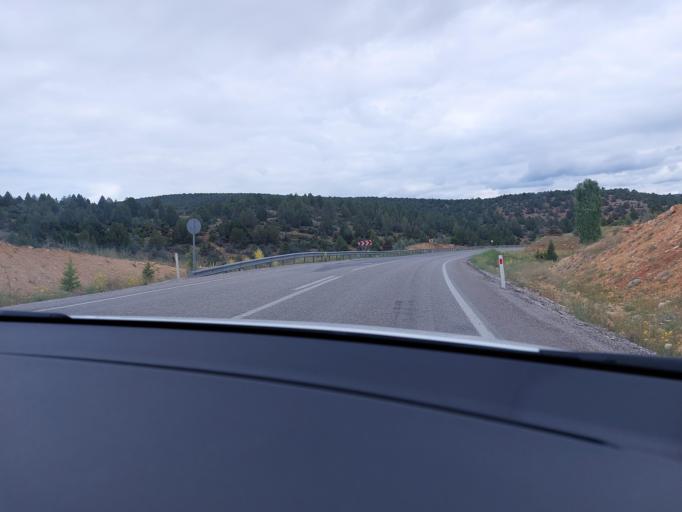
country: TR
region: Konya
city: Doganbey
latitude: 37.8856
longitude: 31.8256
